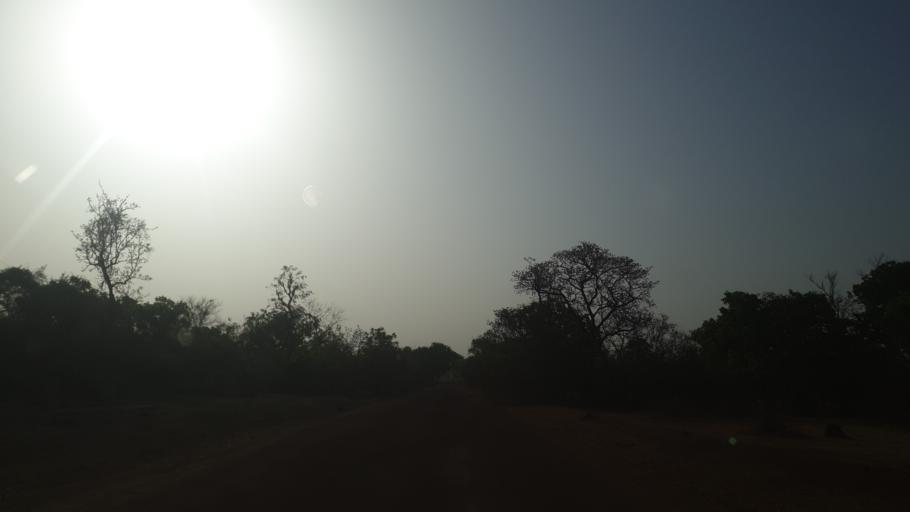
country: ML
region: Sikasso
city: Kolondieba
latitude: 10.8964
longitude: -6.8860
